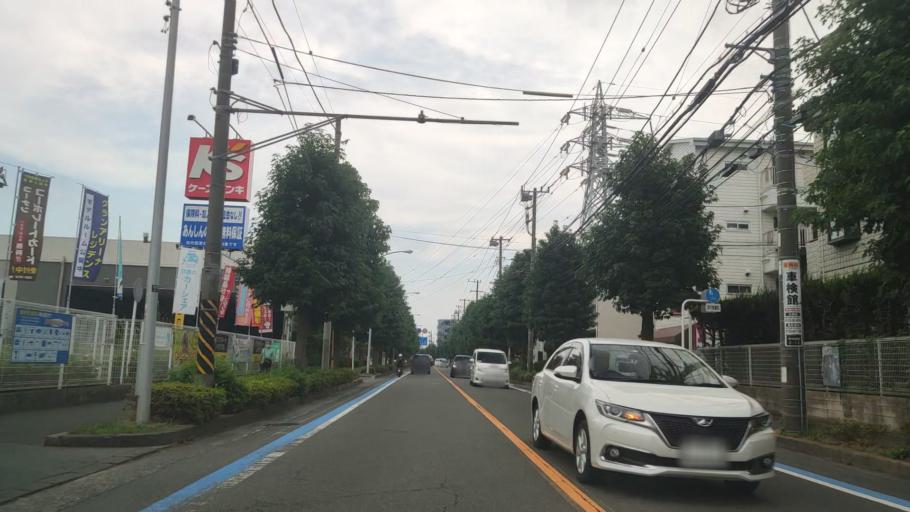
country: JP
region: Kanagawa
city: Minami-rinkan
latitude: 35.5042
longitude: 139.4492
